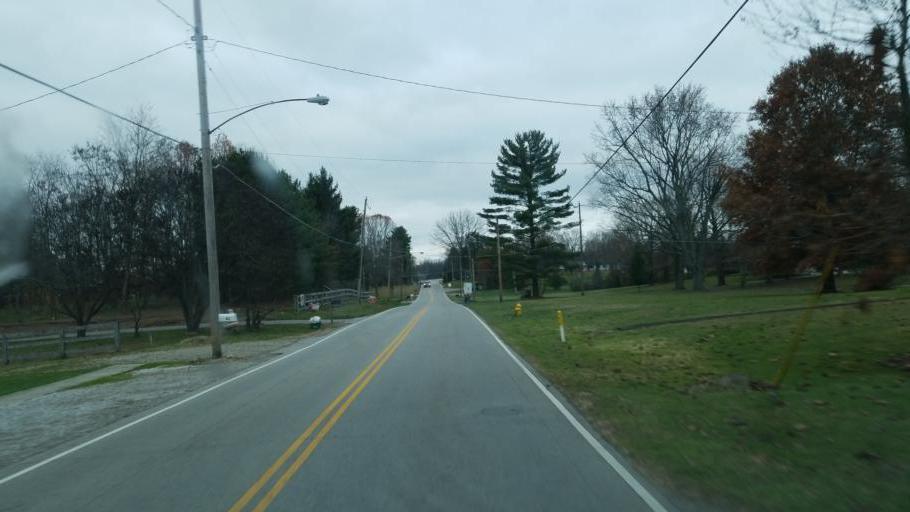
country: US
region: Ohio
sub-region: Delaware County
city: Sunbury
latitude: 40.2234
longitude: -82.8821
